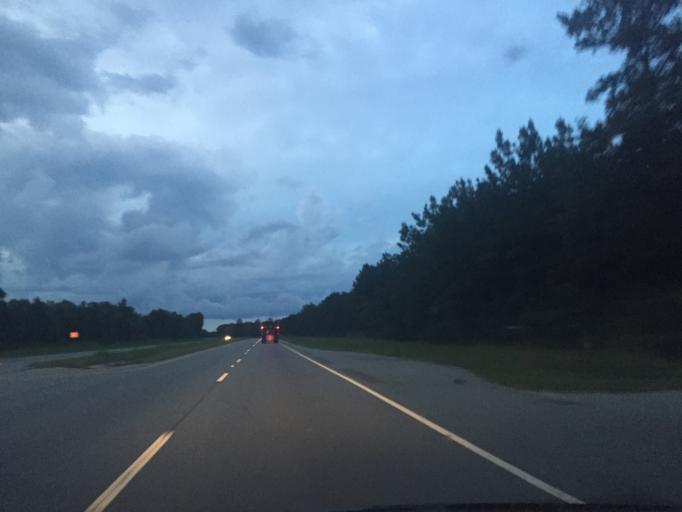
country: US
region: Georgia
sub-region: Liberty County
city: Midway
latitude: 31.8729
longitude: -81.4181
